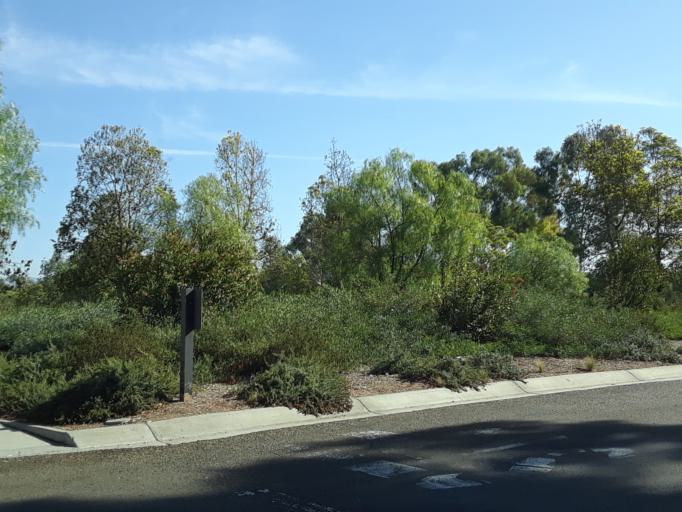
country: US
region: California
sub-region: Orange County
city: Irvine
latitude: 33.6754
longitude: -117.7715
